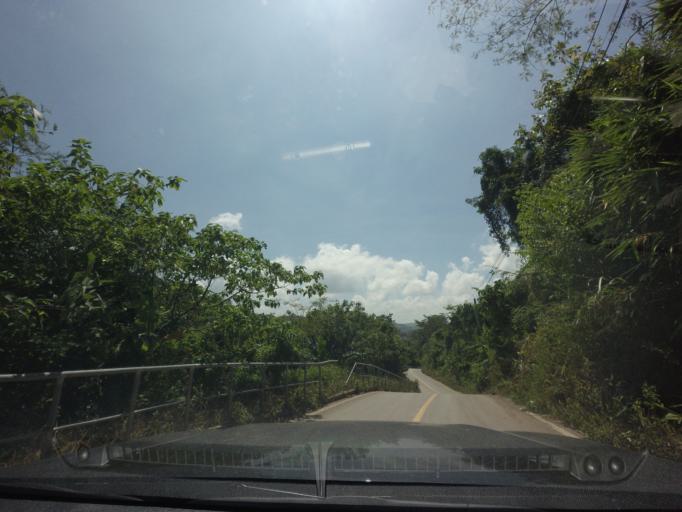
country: TH
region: Phetchabun
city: Khao Kho
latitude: 16.7887
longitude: 101.0486
